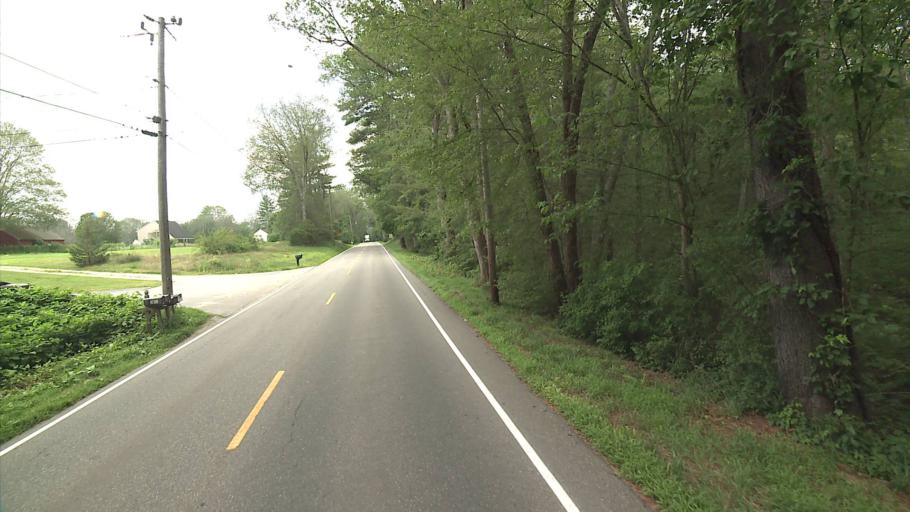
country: US
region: Connecticut
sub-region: Windham County
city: Wauregan
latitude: 41.7626
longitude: -71.9323
